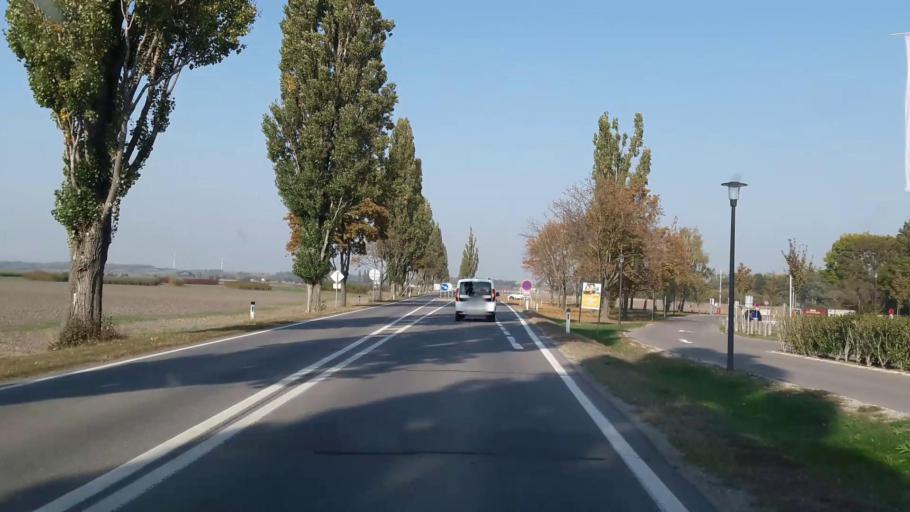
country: AT
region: Lower Austria
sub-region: Politischer Bezirk Ganserndorf
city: Engelhartstetten
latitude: 48.1984
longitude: 16.9006
